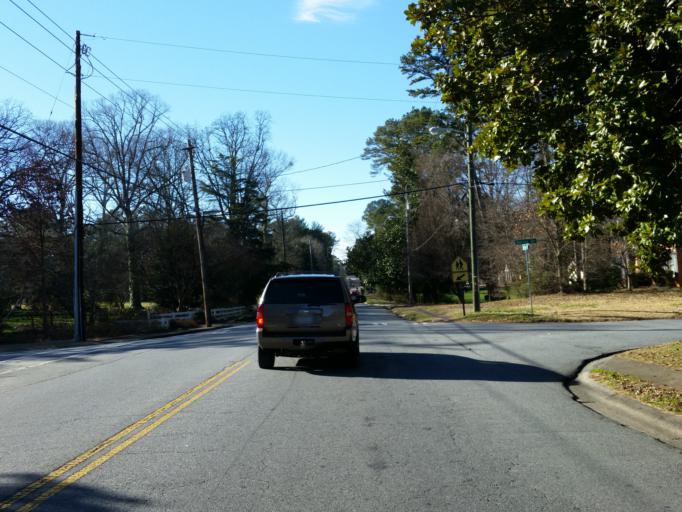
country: US
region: Georgia
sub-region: Cobb County
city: Smyrna
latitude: 33.9417
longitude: -84.4700
